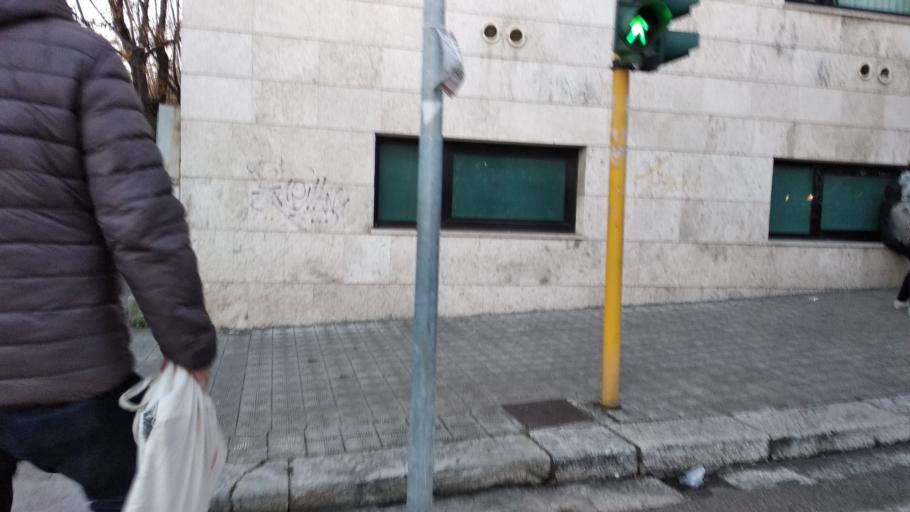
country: IT
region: Calabria
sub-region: Provincia di Reggio Calabria
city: Reggio Calabria
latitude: 38.1143
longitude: 15.6520
